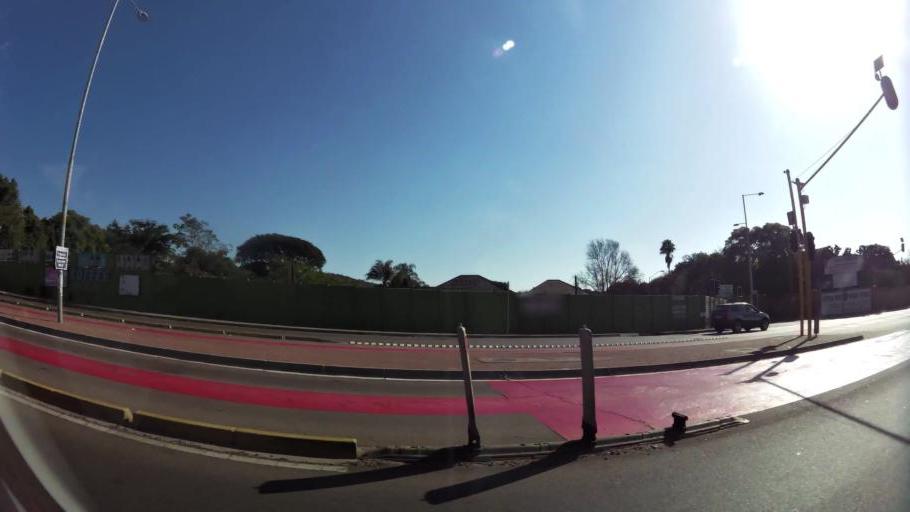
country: ZA
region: Gauteng
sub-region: City of Tshwane Metropolitan Municipality
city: Pretoria
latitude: -25.7289
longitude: 28.1890
